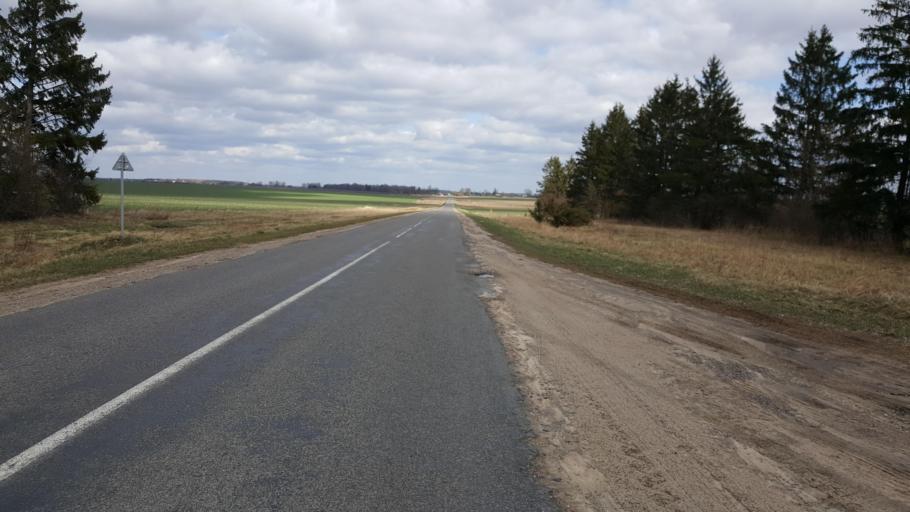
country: BY
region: Brest
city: Vysokaye
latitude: 52.4420
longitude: 23.4878
